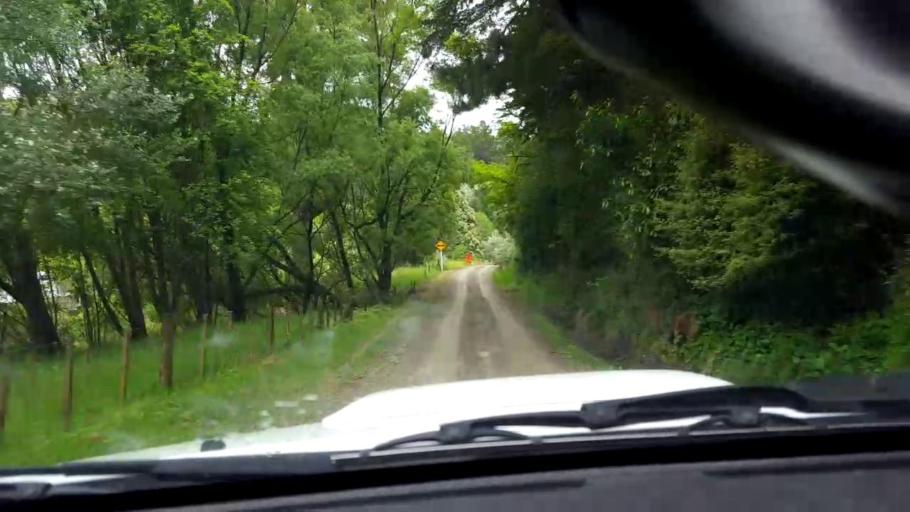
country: NZ
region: Gisborne
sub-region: Gisborne District
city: Gisborne
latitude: -38.3835
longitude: 177.6293
